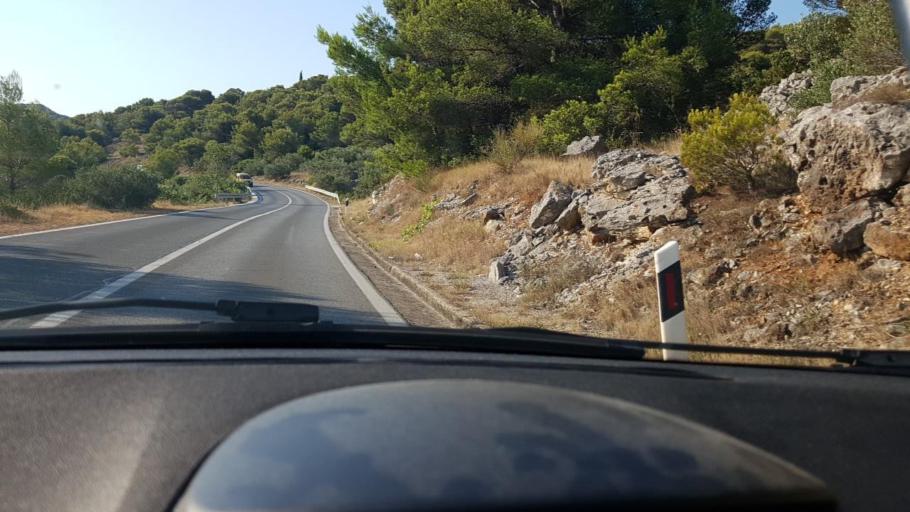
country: HR
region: Sibensko-Kniniska
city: Murter
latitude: 43.8085
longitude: 15.6047
